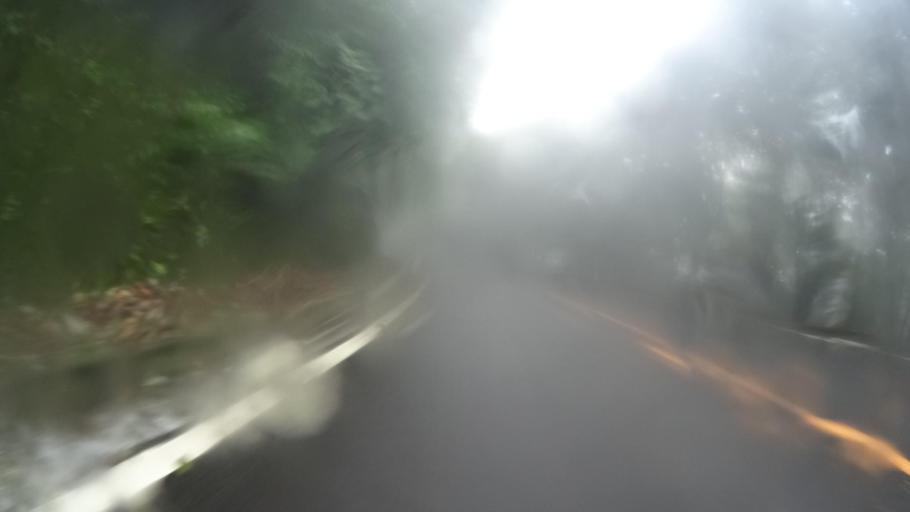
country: JP
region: Yamanashi
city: Uenohara
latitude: 35.7597
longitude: 139.0414
